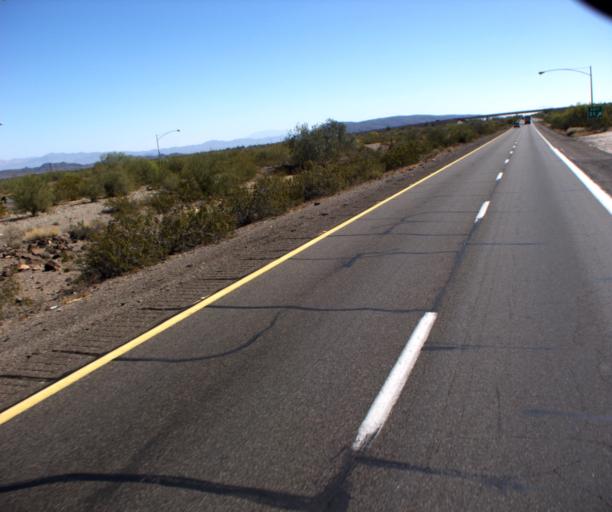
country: US
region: Arizona
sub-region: La Paz County
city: Quartzsite
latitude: 33.6625
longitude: -114.0195
